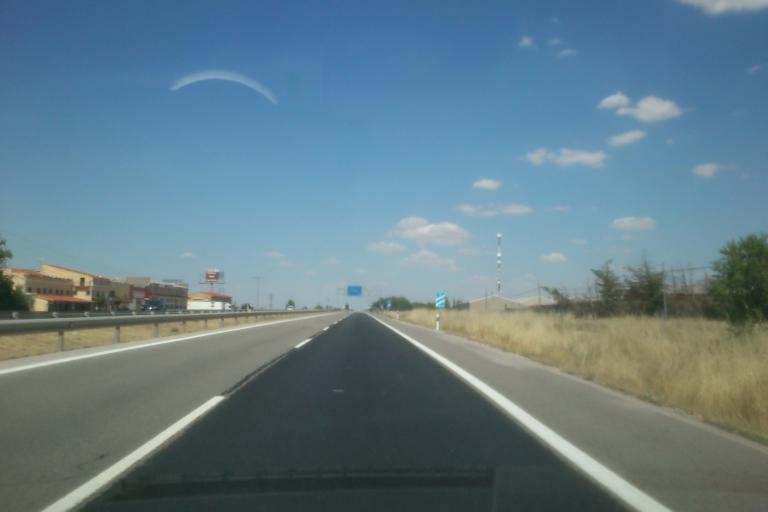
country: ES
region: Castille-La Mancha
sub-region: Provincia de Guadalajara
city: Trijueque
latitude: 40.7729
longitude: -2.9954
